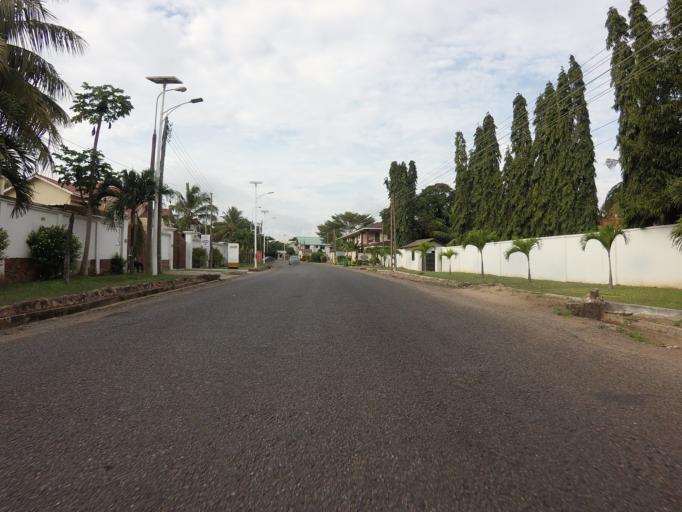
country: GH
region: Greater Accra
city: Accra
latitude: 5.5833
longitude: -0.1693
